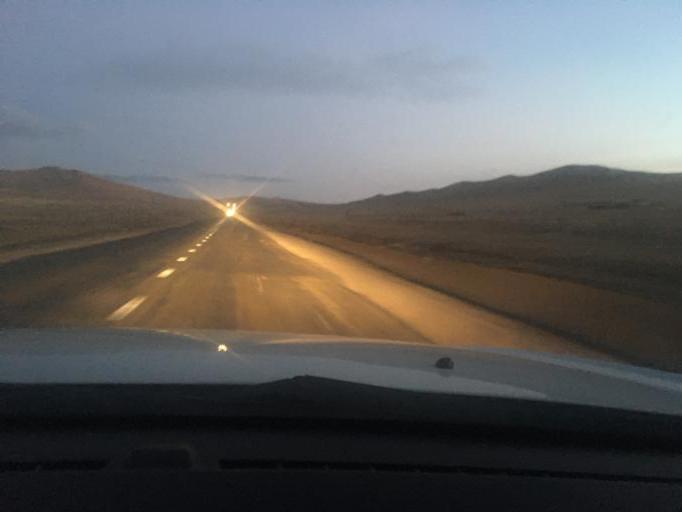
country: MN
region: Ulaanbaatar
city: Ulaanbaatar
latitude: 47.9838
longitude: 106.5669
